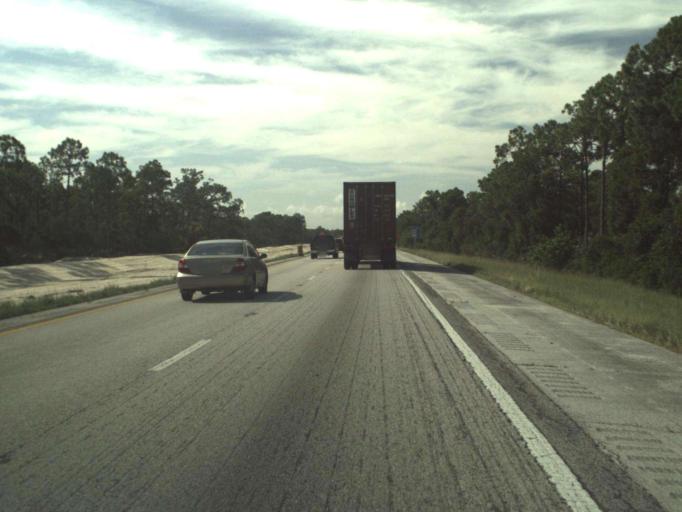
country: US
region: Florida
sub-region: Indian River County
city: West Vero Corridor
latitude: 27.6547
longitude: -80.5250
